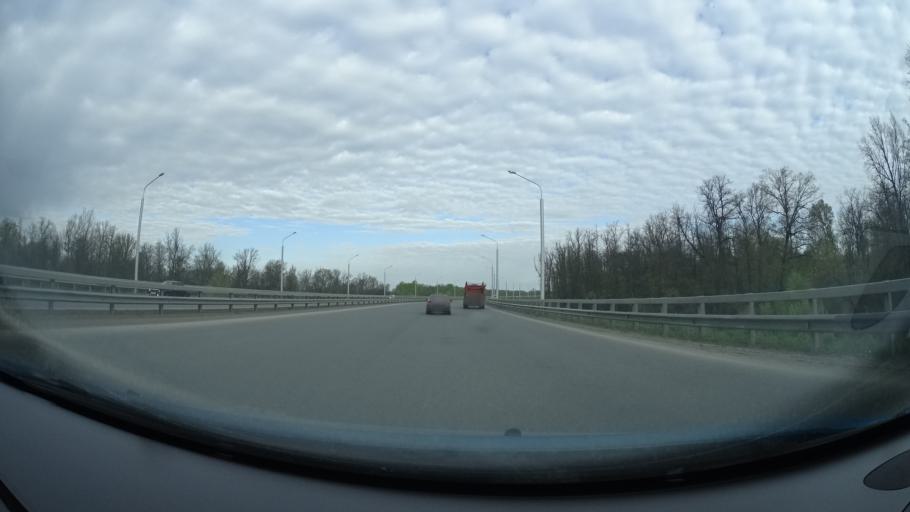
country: RU
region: Bashkortostan
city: Mikhaylovka
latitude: 54.7806
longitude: 55.9186
